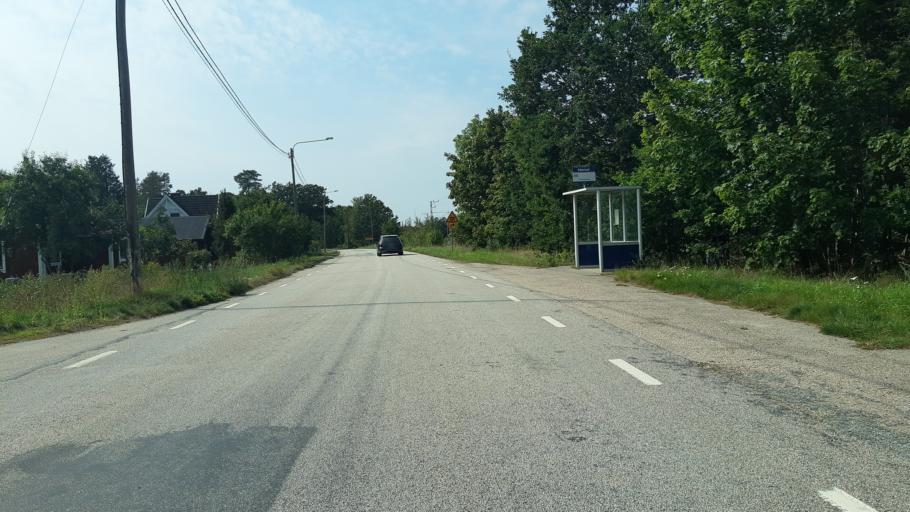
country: SE
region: Blekinge
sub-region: Ronneby Kommun
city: Kallinge
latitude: 56.2186
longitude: 15.3666
